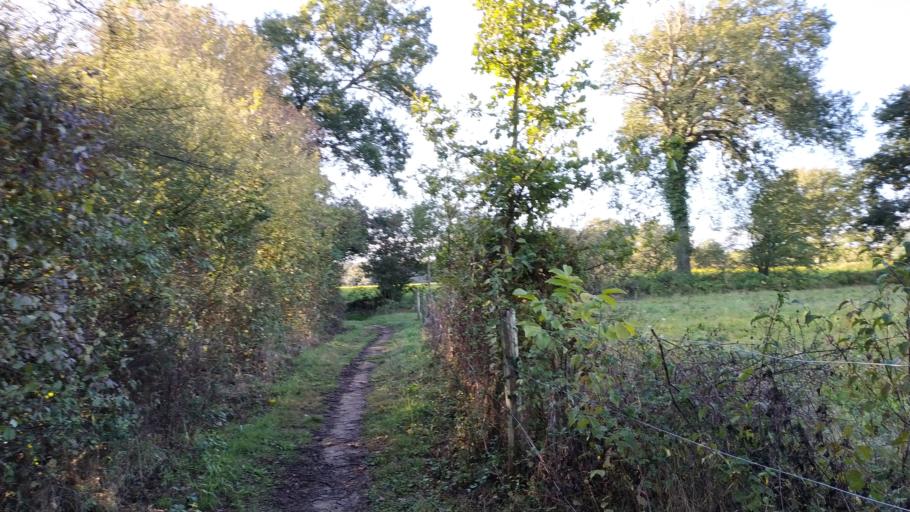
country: FR
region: Brittany
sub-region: Departement d'Ille-et-Vilaine
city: Chantepie
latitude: 48.0781
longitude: -1.6206
